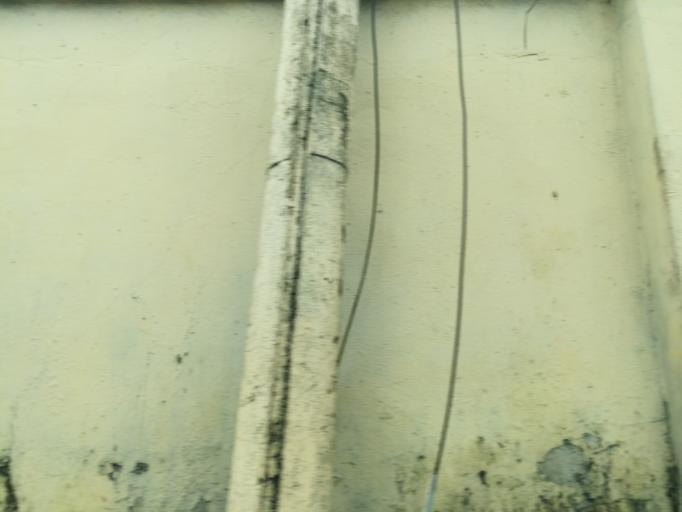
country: NG
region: Rivers
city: Port Harcourt
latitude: 4.8564
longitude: 7.0394
